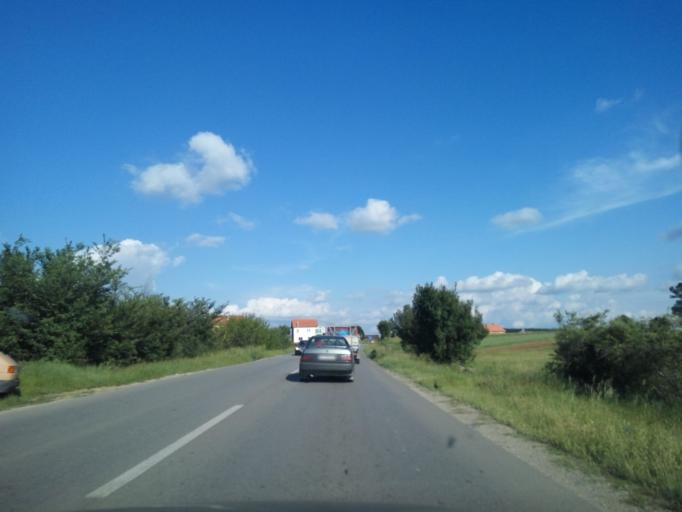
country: XK
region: Pec
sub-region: Komuna e Klines
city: Klina
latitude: 42.5941
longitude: 20.6586
